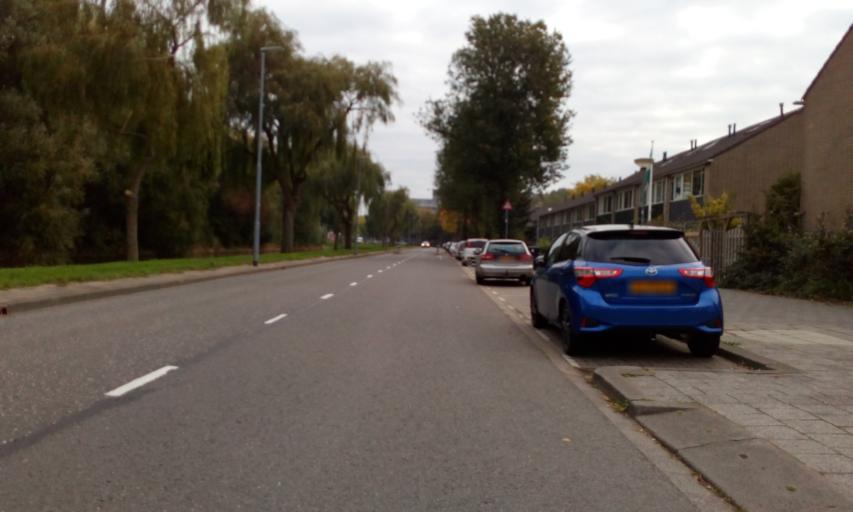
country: NL
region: South Holland
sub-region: Gemeente Spijkenisse
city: Spijkenisse
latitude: 51.8509
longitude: 4.3637
